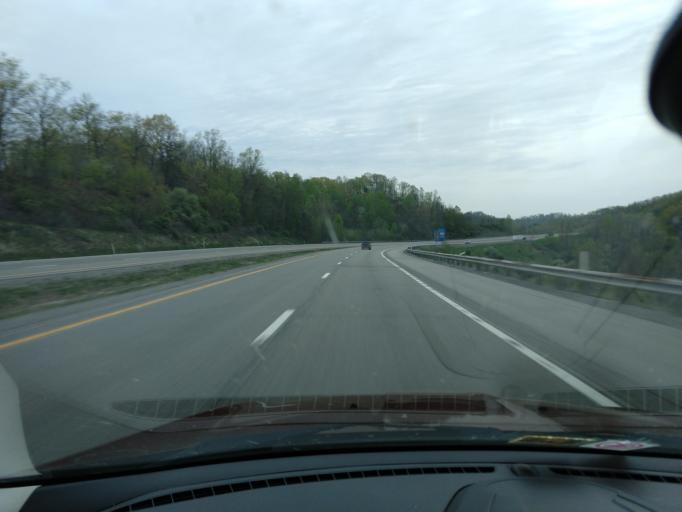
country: US
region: West Virginia
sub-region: Lewis County
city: Weston
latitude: 38.9517
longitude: -80.5345
